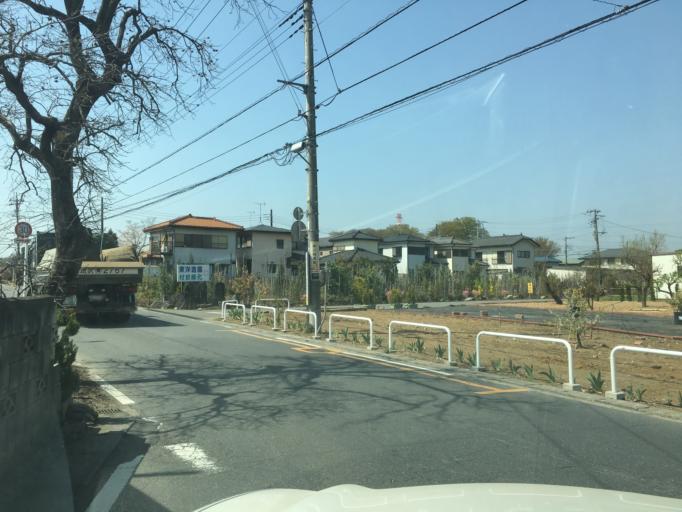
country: JP
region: Saitama
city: Sayama
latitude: 35.8568
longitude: 139.4614
